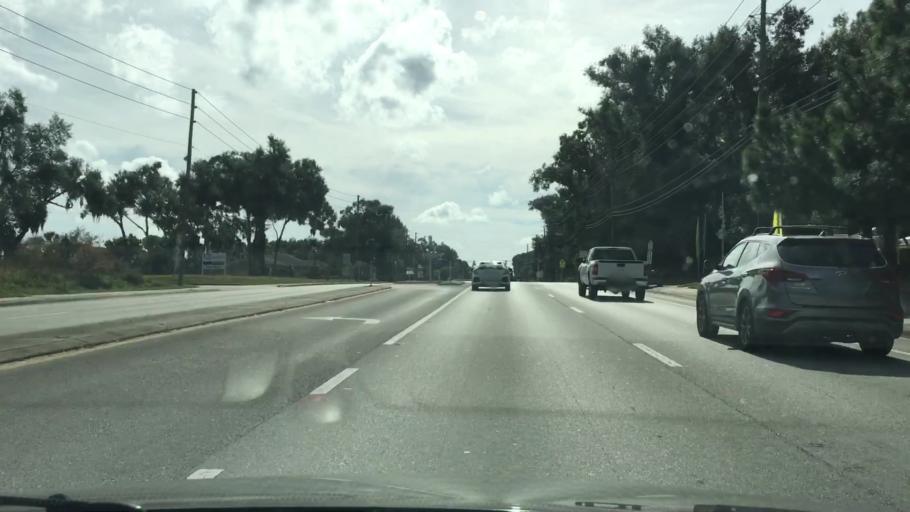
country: US
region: Florida
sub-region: Volusia County
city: North DeLand
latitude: 29.0448
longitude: -81.3248
